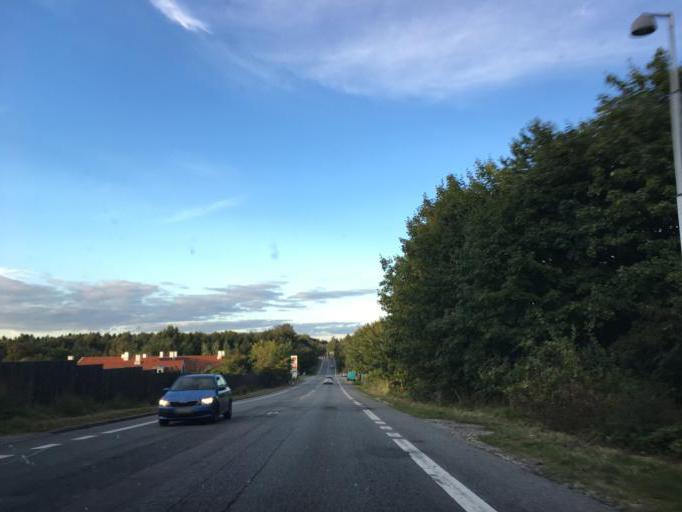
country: DK
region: Capital Region
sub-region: Horsholm Kommune
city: Horsholm
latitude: 55.8626
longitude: 12.4957
